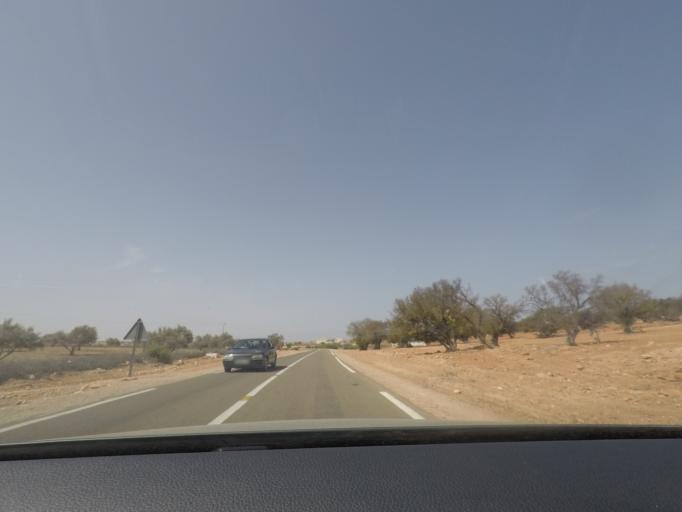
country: MA
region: Marrakech-Tensift-Al Haouz
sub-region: Essaouira
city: Tamanar
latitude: 31.0499
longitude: -9.6617
